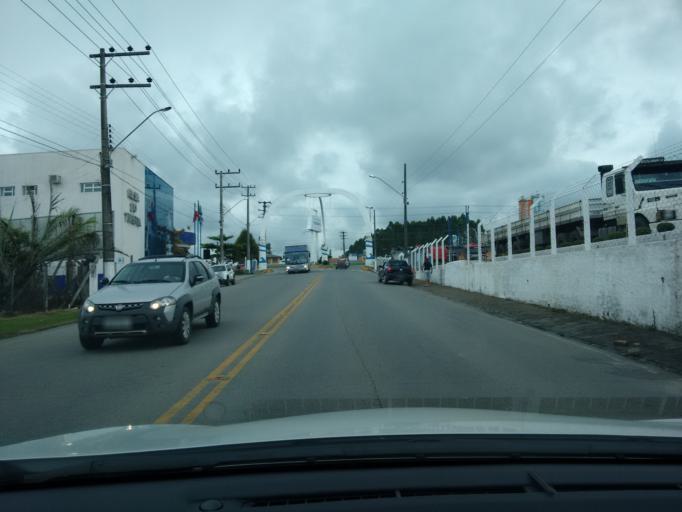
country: BR
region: Santa Catarina
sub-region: Penha
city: Penha
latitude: -26.7621
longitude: -48.6852
